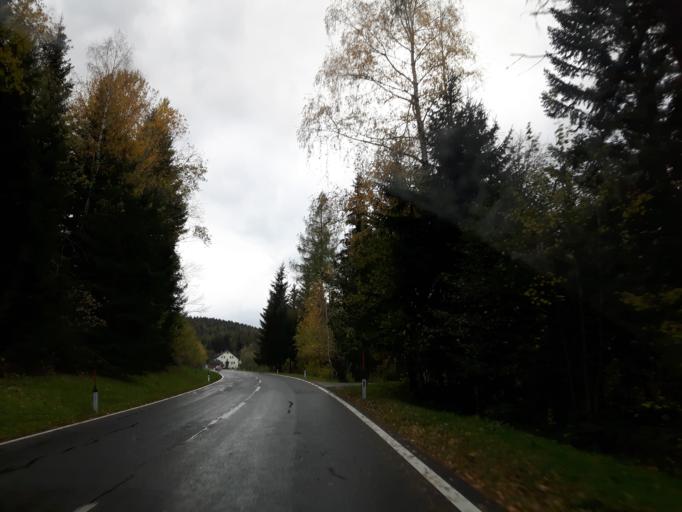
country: AT
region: Styria
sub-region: Politischer Bezirk Deutschlandsberg
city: Sankt Oswald ob Eibiswald
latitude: 46.7037
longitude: 15.1319
